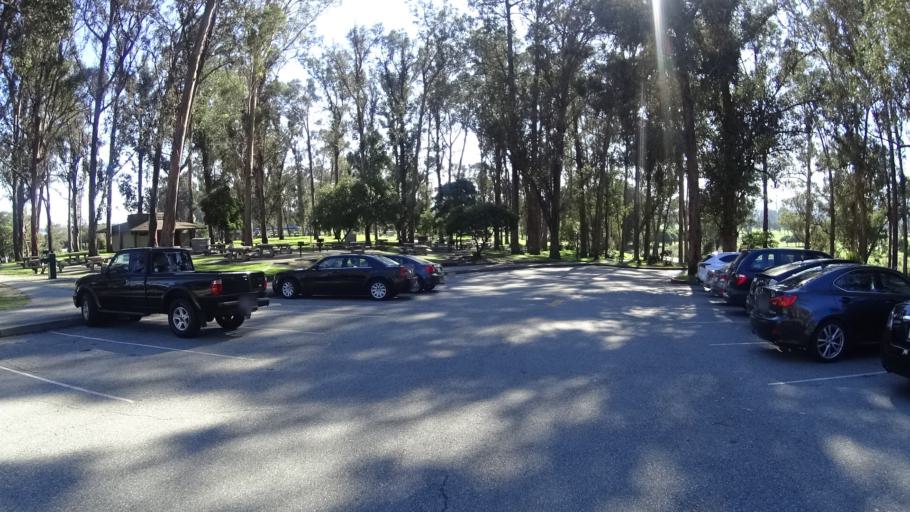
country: US
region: California
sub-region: San Mateo County
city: San Mateo
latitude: 37.5890
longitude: -122.3198
